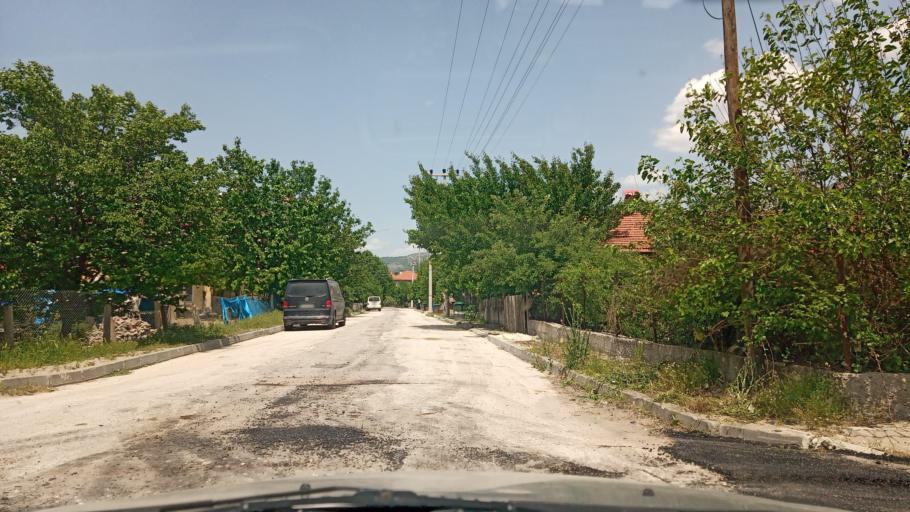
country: TR
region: Bolu
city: Seben
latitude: 40.4102
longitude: 31.5759
